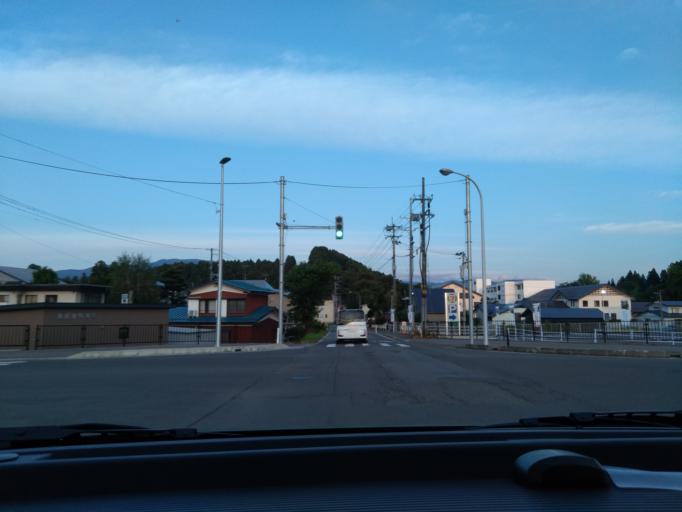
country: JP
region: Akita
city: Kakunodatemachi
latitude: 39.5913
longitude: 140.5596
